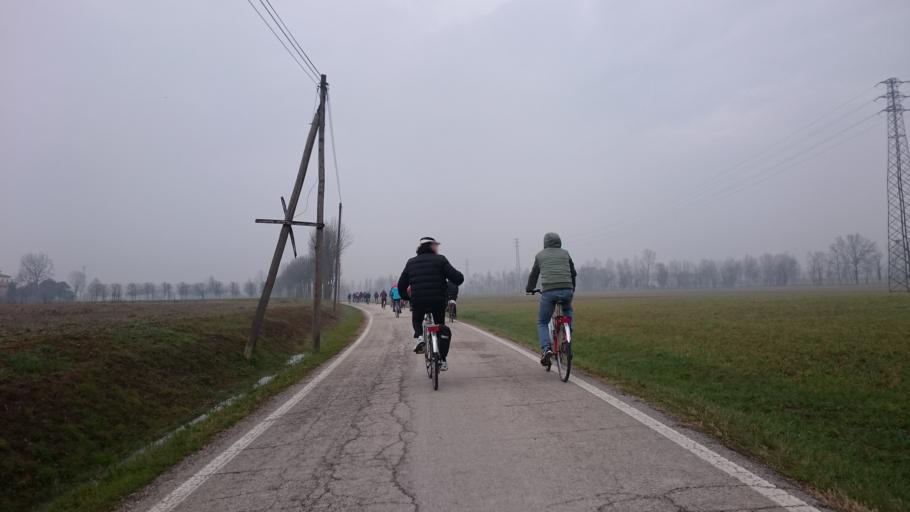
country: IT
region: Veneto
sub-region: Provincia di Vicenza
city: Montegalda
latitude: 45.4758
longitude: 11.6670
